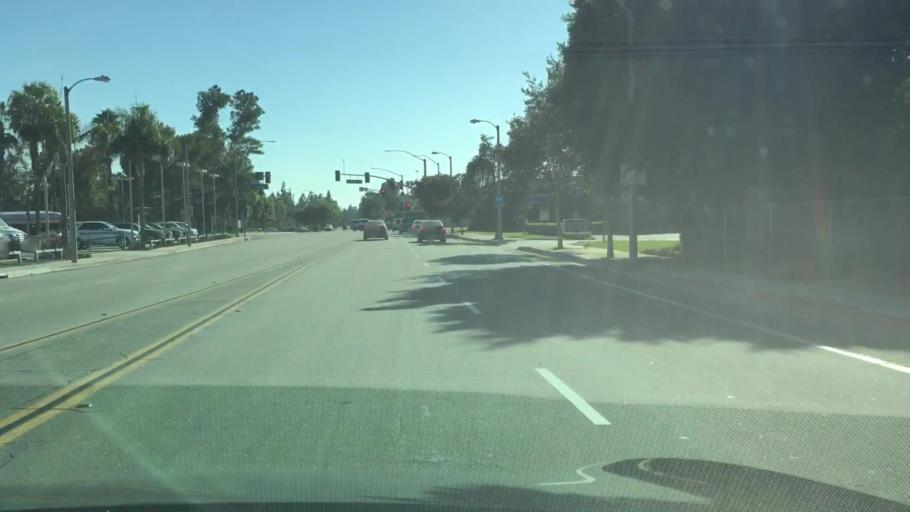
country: US
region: California
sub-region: Los Angeles County
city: Arcadia
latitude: 34.1409
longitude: -118.0344
